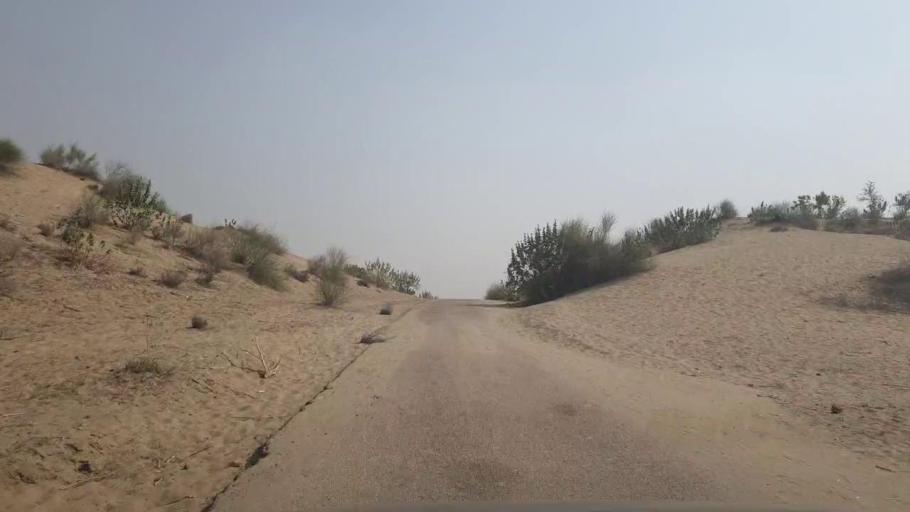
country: PK
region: Sindh
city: Chor
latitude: 25.5906
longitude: 70.0055
